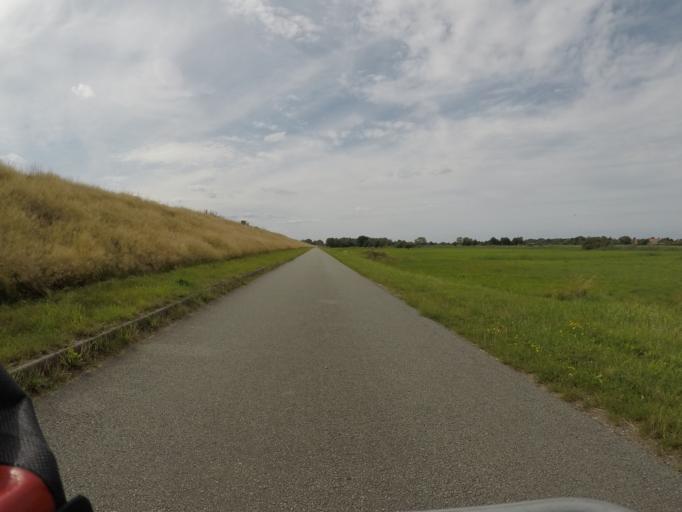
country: DE
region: Lower Saxony
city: Winsen
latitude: 53.3782
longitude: 10.2363
